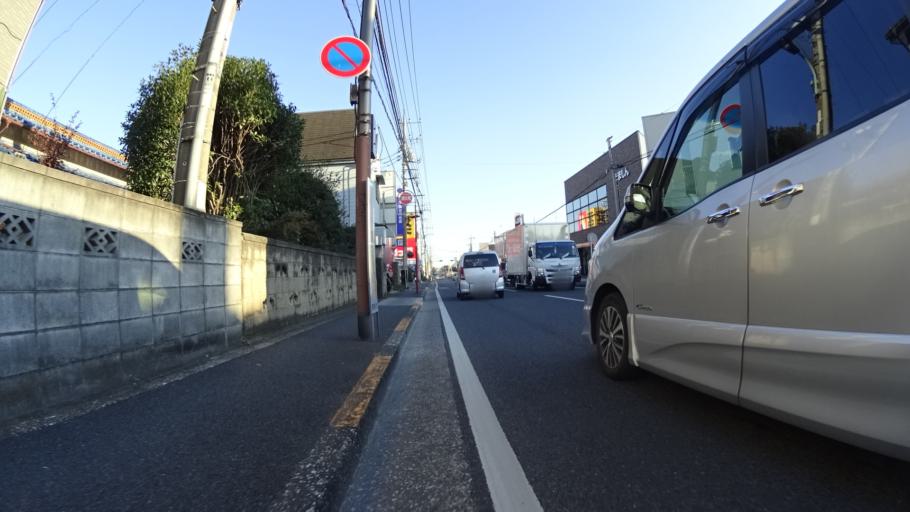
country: JP
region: Tokyo
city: Hachioji
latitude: 35.6725
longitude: 139.2967
